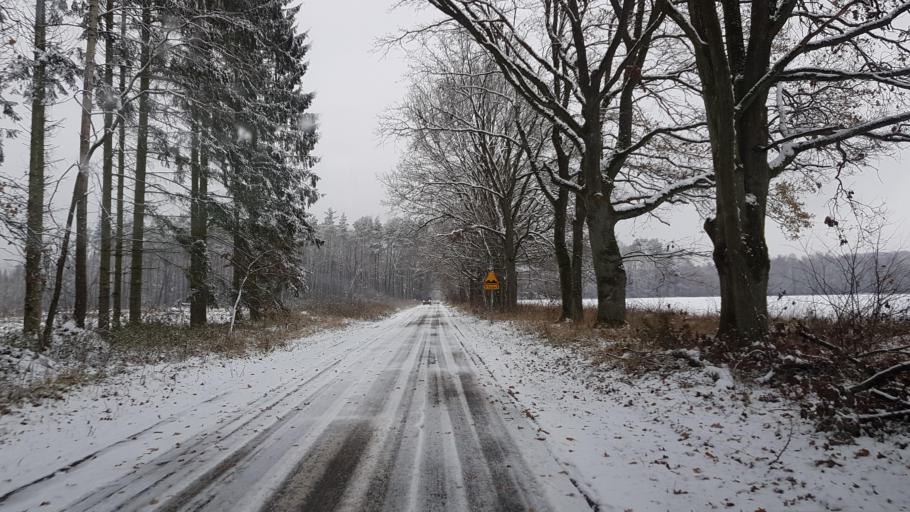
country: PL
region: West Pomeranian Voivodeship
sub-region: Powiat lobeski
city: Resko
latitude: 53.7764
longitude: 15.5318
